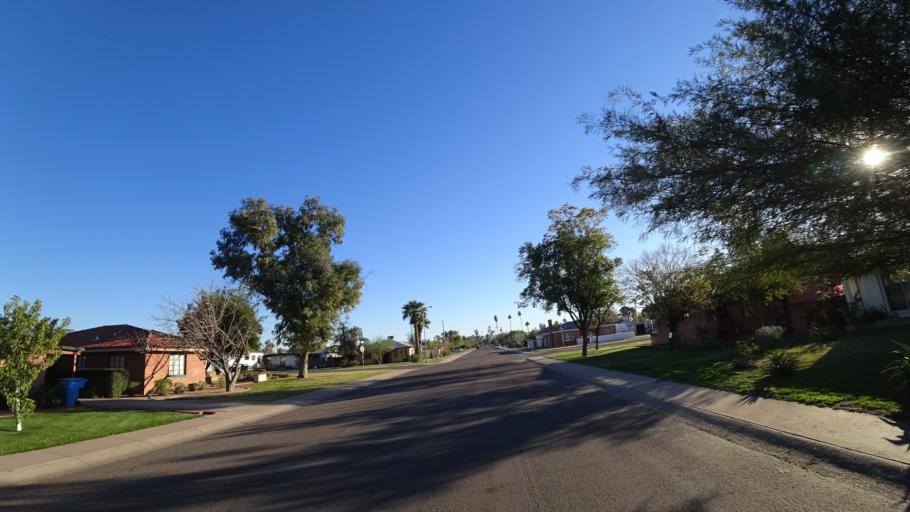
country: US
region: Arizona
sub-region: Maricopa County
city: Phoenix
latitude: 33.4846
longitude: -112.0957
